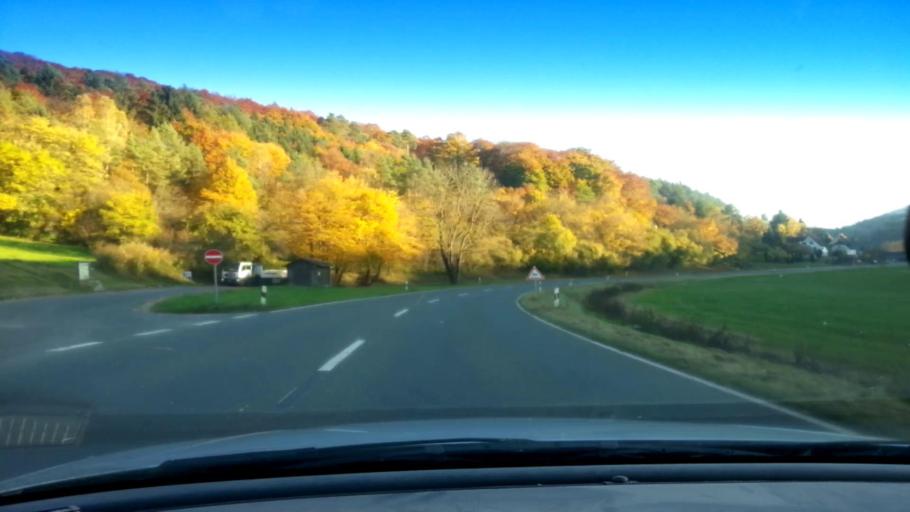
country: DE
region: Bavaria
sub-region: Upper Franconia
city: Heiligenstadt
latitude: 49.8618
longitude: 11.1768
